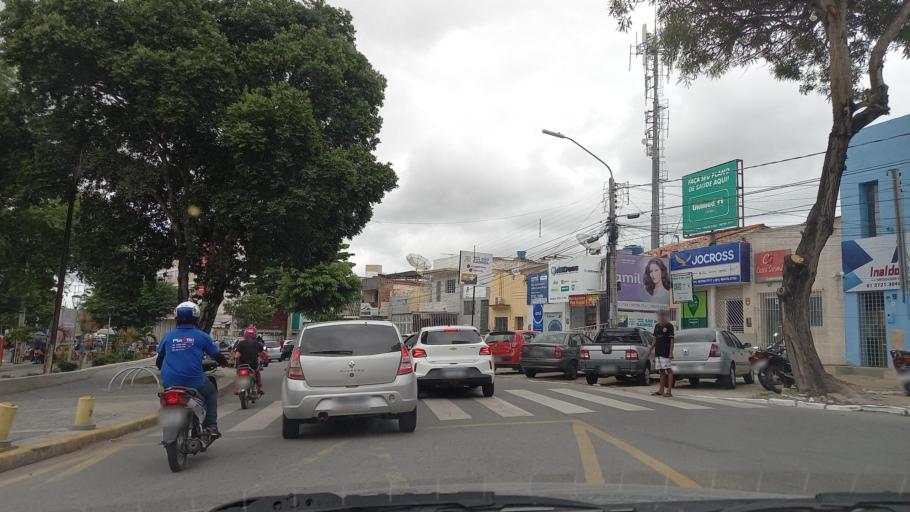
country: BR
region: Pernambuco
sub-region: Caruaru
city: Caruaru
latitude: -8.2821
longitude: -35.9732
